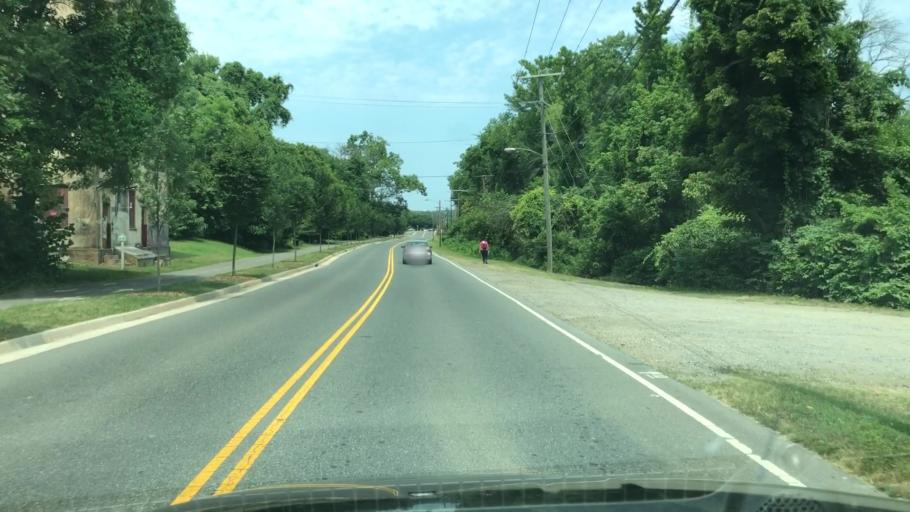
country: US
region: Virginia
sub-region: City of Fredericksburg
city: Fredericksburg
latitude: 38.3123
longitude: -77.4652
